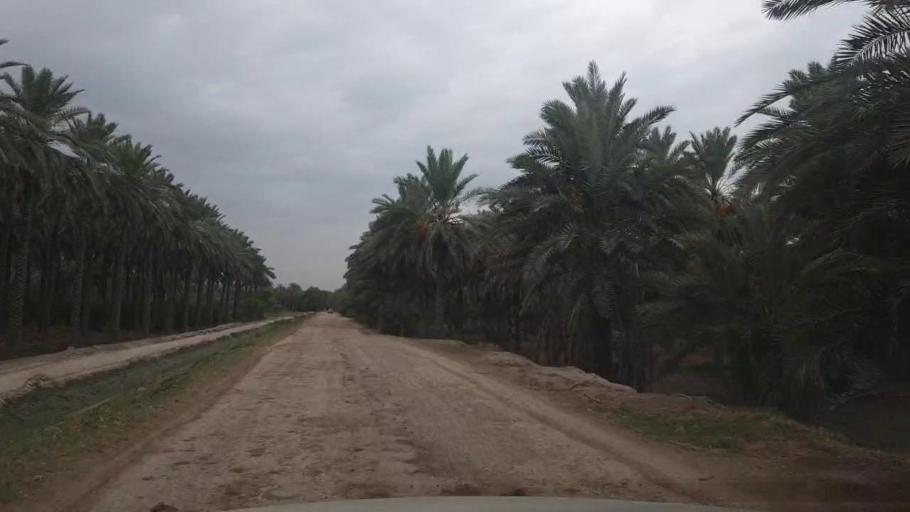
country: PK
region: Sindh
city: Khairpur
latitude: 27.6010
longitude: 68.8154
